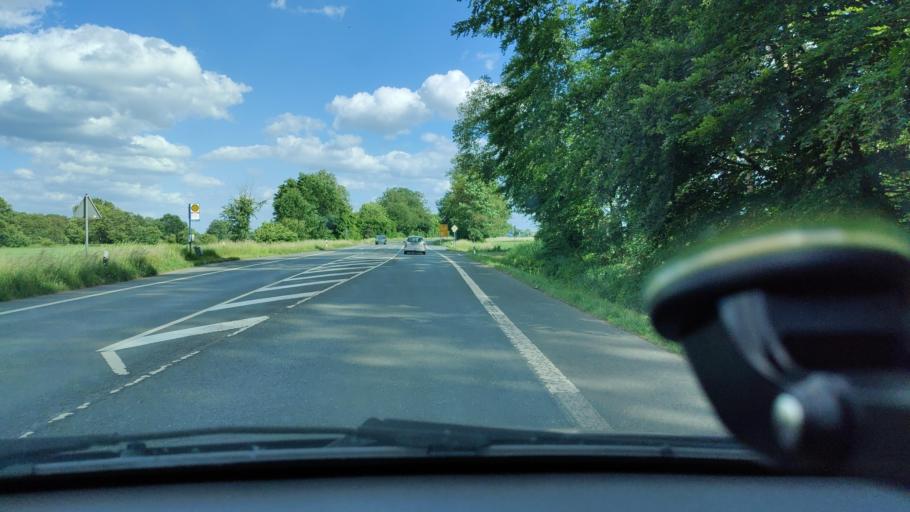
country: DE
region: North Rhine-Westphalia
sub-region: Regierungsbezirk Munster
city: Gescher
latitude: 51.9686
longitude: 6.9755
